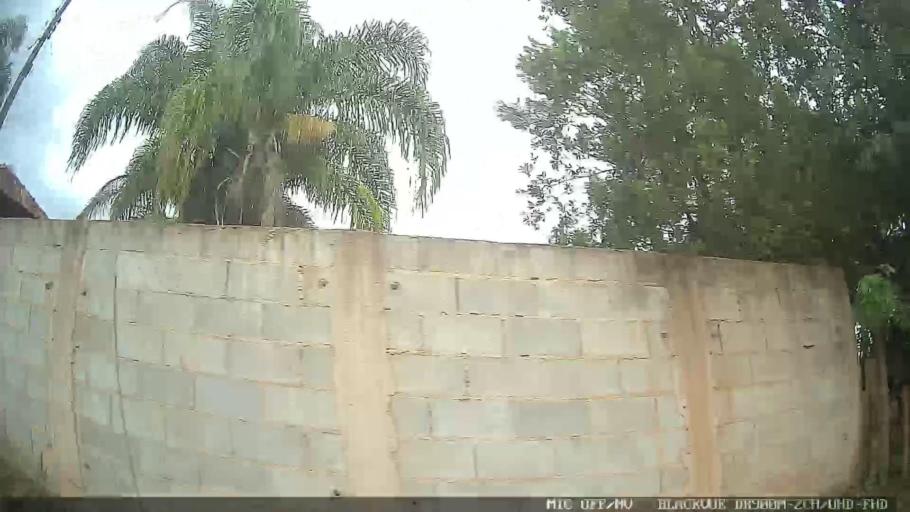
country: BR
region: Sao Paulo
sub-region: Aruja
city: Aruja
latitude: -23.4163
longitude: -46.2297
